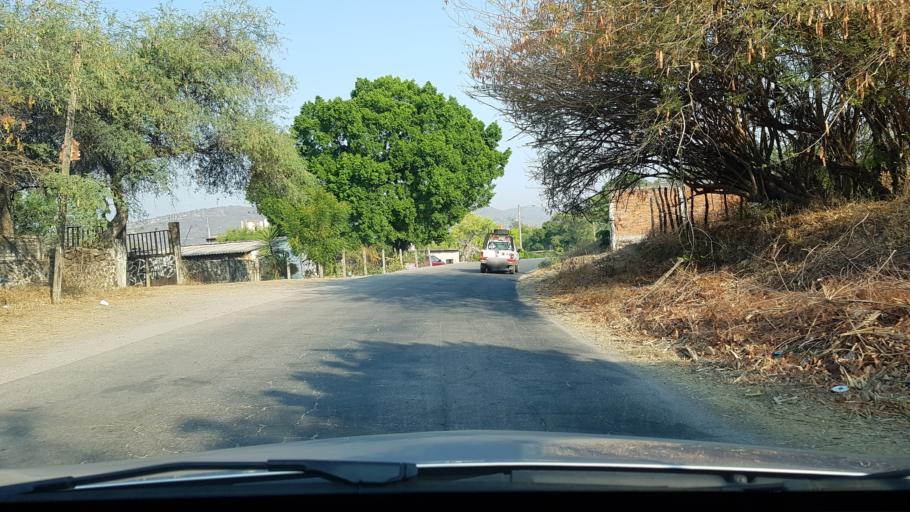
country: MX
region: Morelos
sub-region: Tlaltizapan de Zapata
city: Colonia Palo Prieto (Chipitongo)
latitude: 18.6967
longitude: -99.1029
